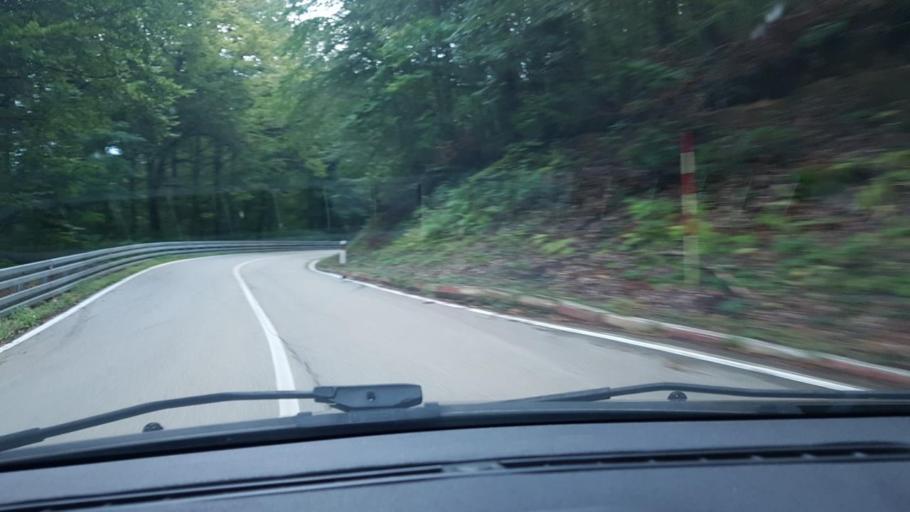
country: HR
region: Grad Zagreb
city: Kasina
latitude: 45.9405
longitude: 15.9681
